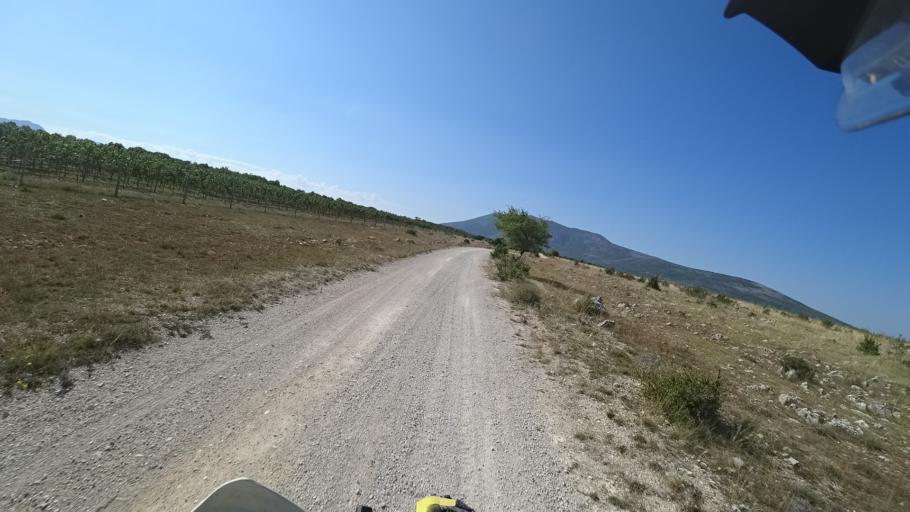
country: HR
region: Sibensko-Kniniska
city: Knin
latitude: 43.9902
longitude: 16.1924
